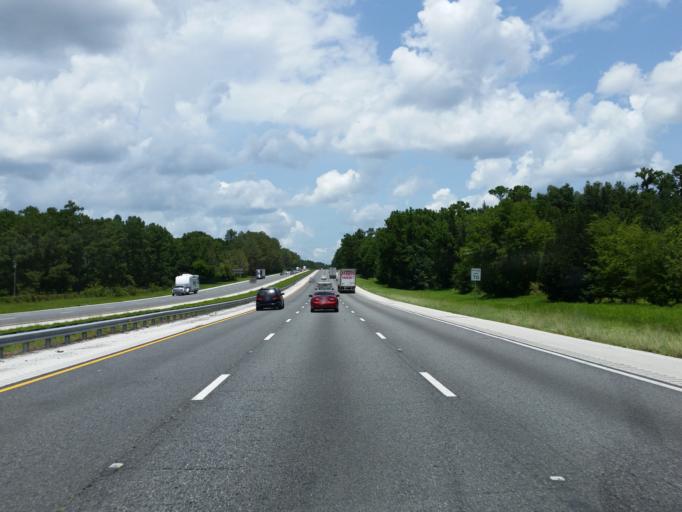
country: US
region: Florida
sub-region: Marion County
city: Citra
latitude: 29.4147
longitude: -82.2532
